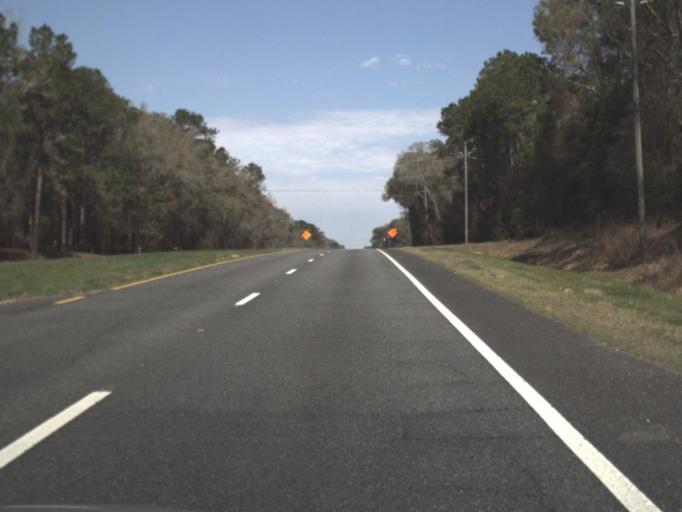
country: US
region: Florida
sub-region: Gadsden County
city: Havana
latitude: 30.5629
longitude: -84.3898
